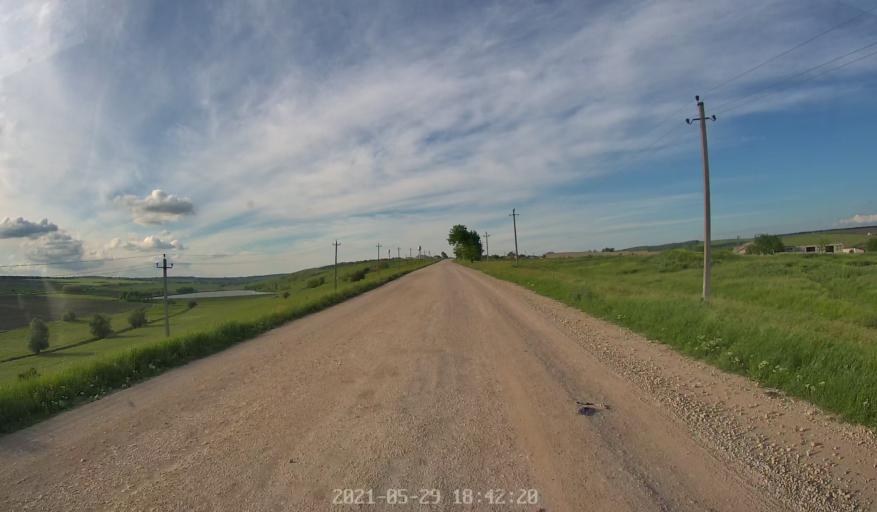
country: MD
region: Chisinau
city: Singera
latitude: 46.8114
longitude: 28.9618
